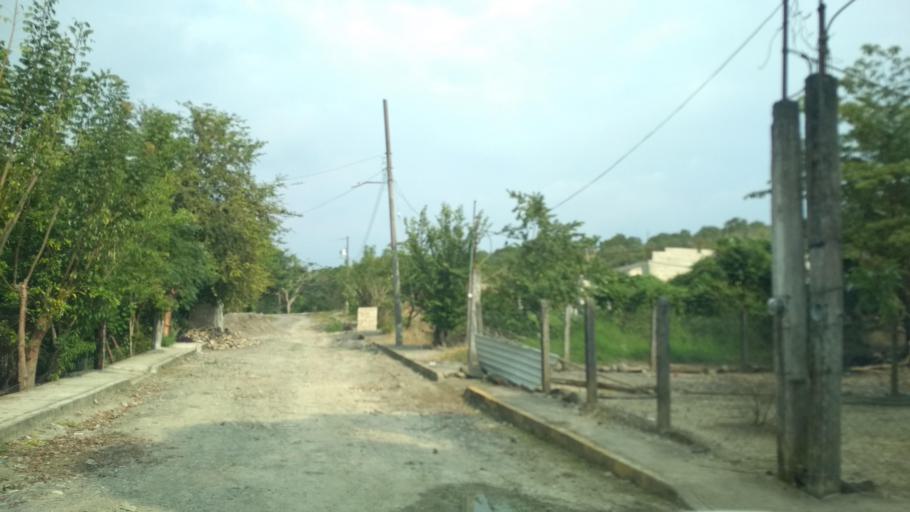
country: MM
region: Kayah
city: Loikaw
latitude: 20.2353
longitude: 97.2769
